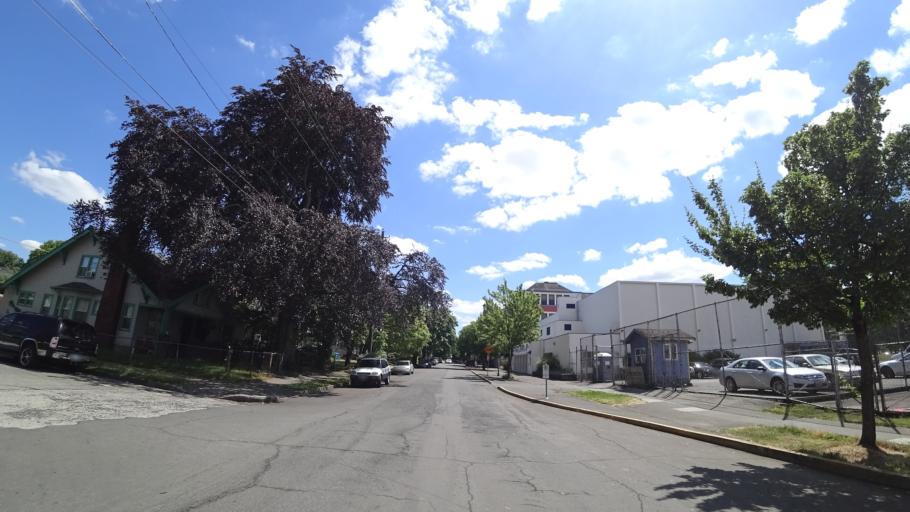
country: US
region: Oregon
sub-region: Multnomah County
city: Portland
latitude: 45.5618
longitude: -122.6711
